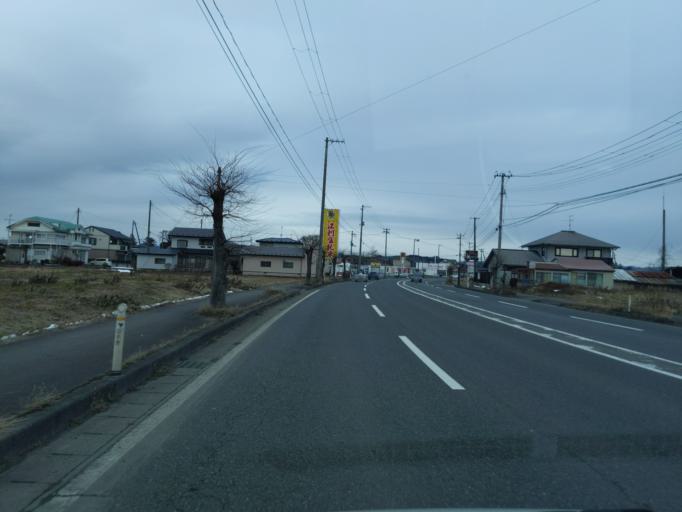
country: JP
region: Iwate
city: Mizusawa
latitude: 39.1774
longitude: 141.1600
